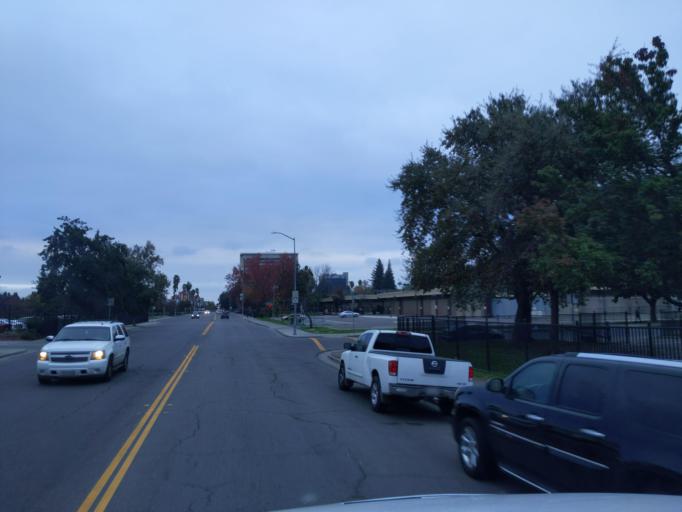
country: US
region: California
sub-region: San Joaquin County
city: Stockton
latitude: 37.9525
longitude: -121.2970
